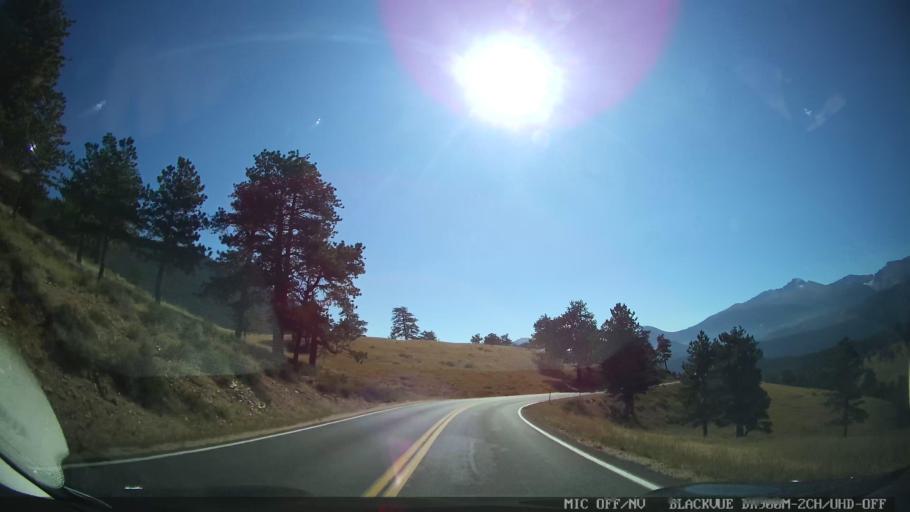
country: US
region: Colorado
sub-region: Larimer County
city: Estes Park
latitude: 40.3830
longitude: -105.6057
